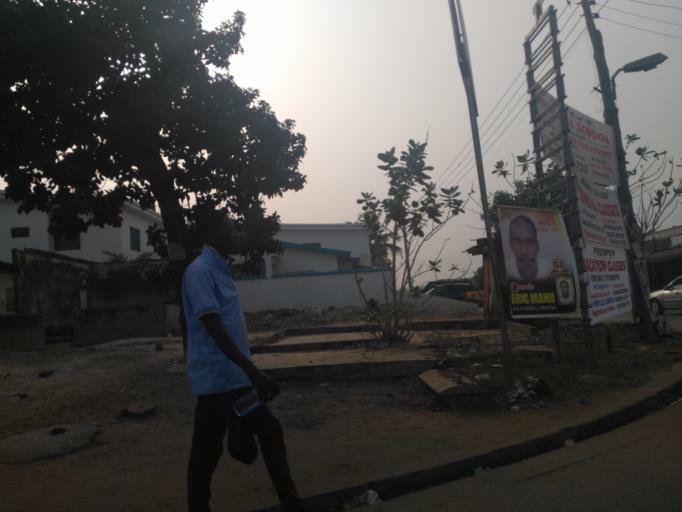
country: GH
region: Ashanti
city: Kumasi
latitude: 6.6872
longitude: -1.6447
